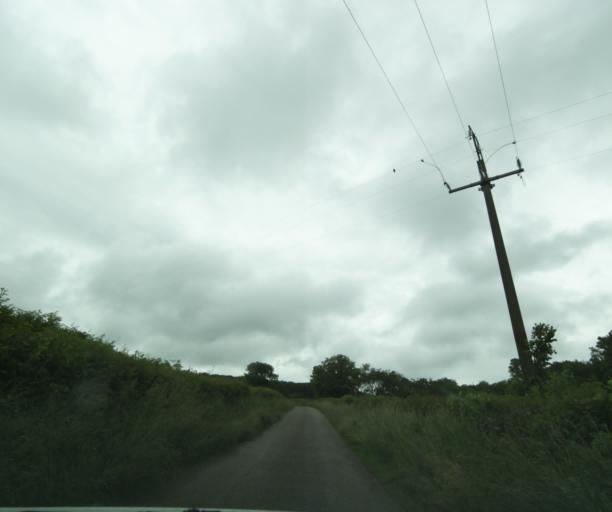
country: FR
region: Bourgogne
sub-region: Departement de Saone-et-Loire
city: Charolles
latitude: 46.4974
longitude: 4.2820
